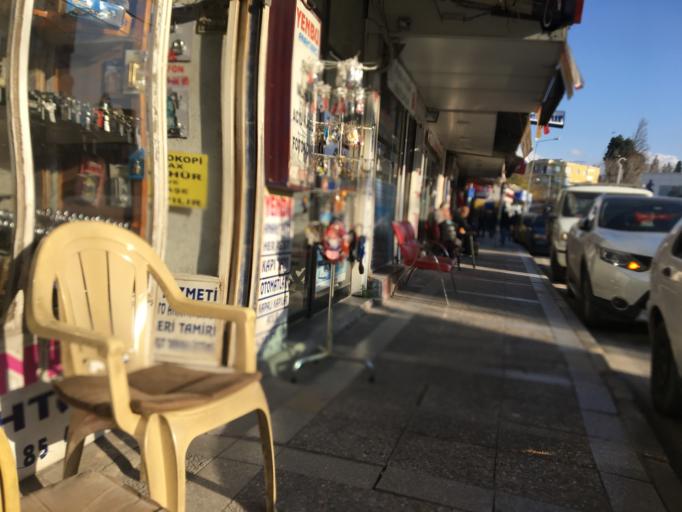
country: TR
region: Izmir
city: Buca
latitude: 38.3884
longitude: 27.1726
